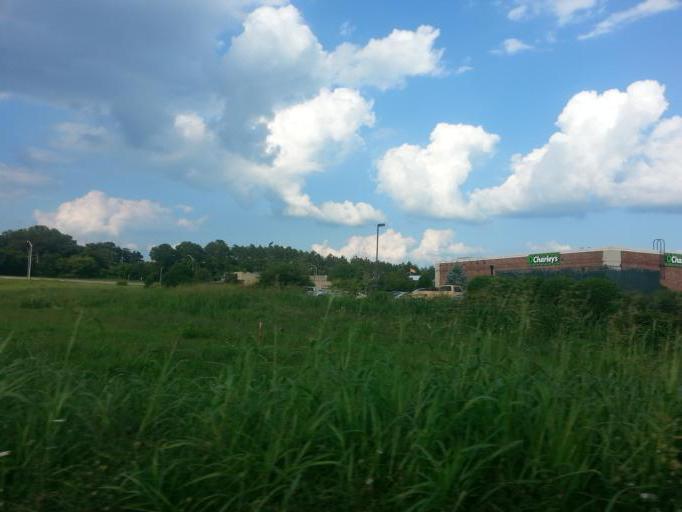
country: US
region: Tennessee
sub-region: Blount County
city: Alcoa
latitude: 35.7812
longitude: -83.9903
